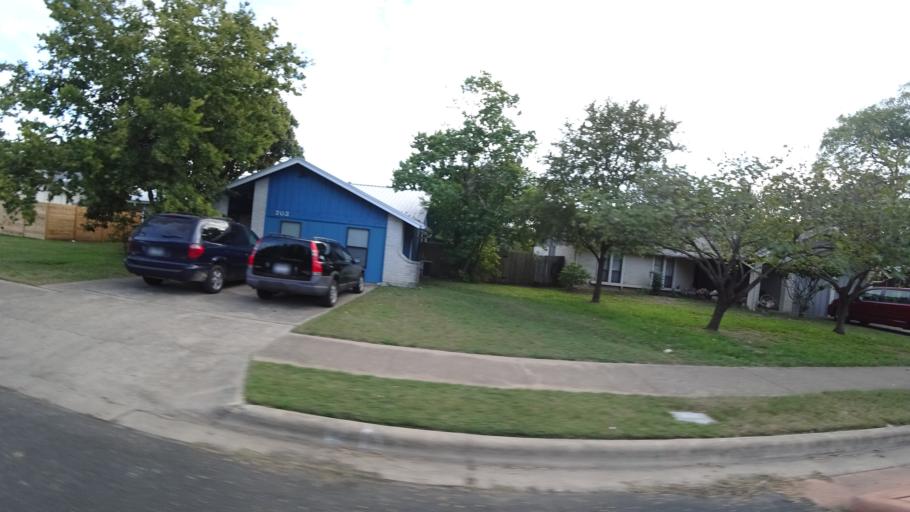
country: US
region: Texas
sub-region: Travis County
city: Austin
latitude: 30.2038
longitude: -97.7655
